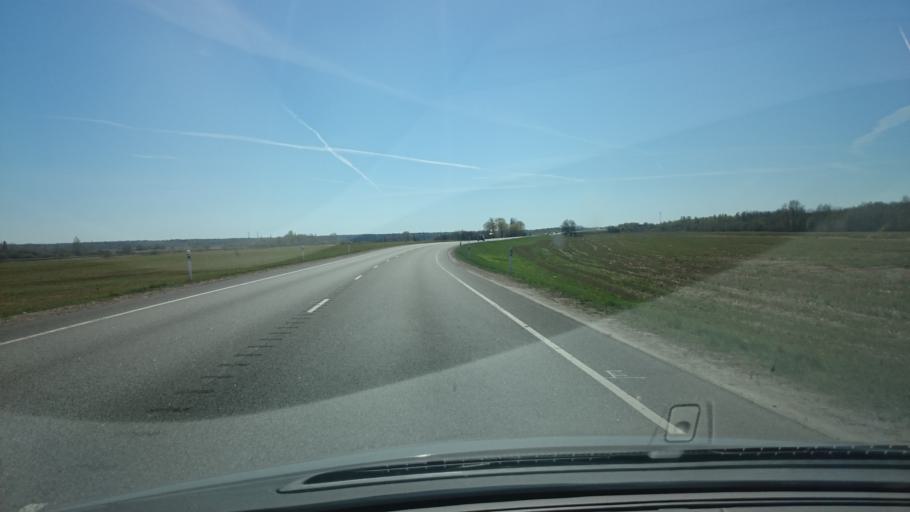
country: EE
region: Ida-Virumaa
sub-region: Narva-Joesuu linn
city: Narva-Joesuu
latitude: 59.4024
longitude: 28.0154
